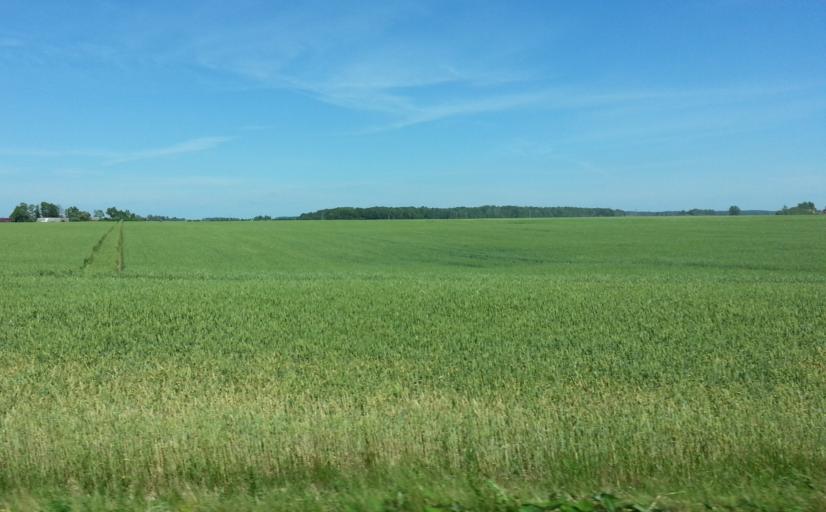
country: LT
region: Panevezys
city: Pasvalys
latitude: 56.1737
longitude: 24.4420
